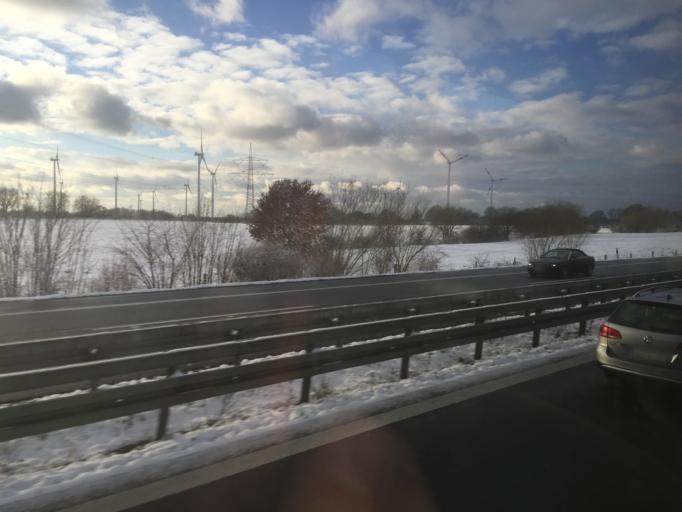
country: DE
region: Brandenburg
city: Gerdshagen
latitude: 53.2597
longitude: 12.1555
